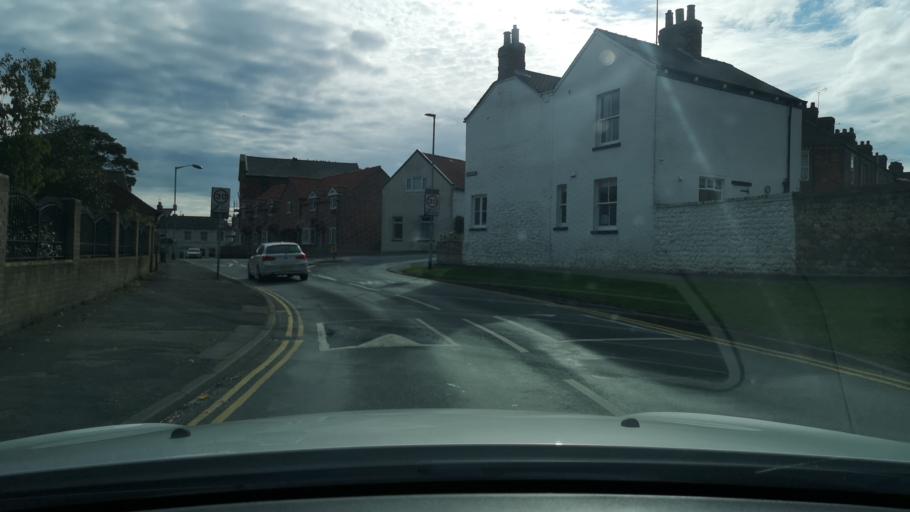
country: GB
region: England
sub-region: East Riding of Yorkshire
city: Hornsea
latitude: 53.9123
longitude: -0.1751
